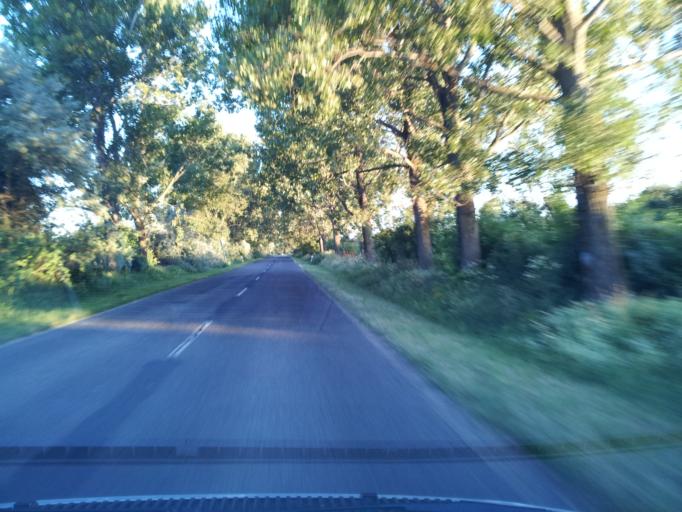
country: HU
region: Veszprem
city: Szentkiralyszabadja
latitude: 47.0479
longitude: 17.9302
